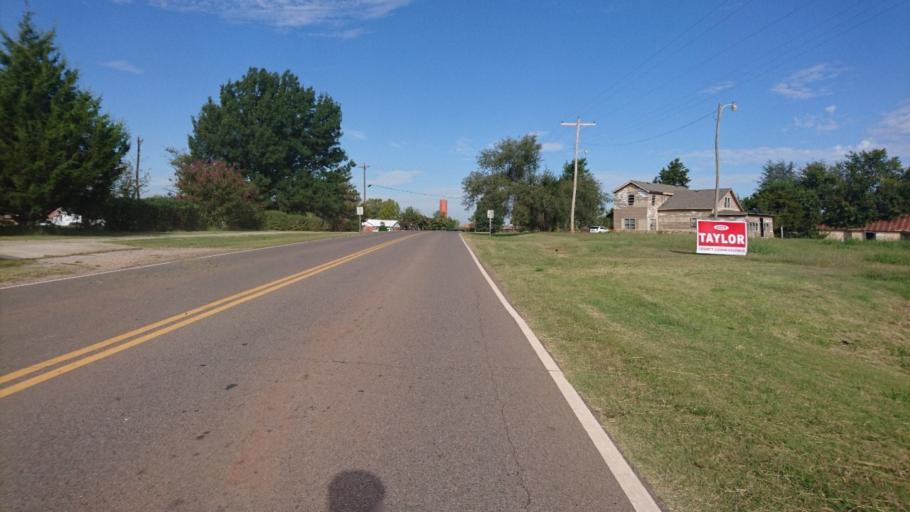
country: US
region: Oklahoma
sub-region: Oklahoma County
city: Luther
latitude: 35.6859
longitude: -97.0606
